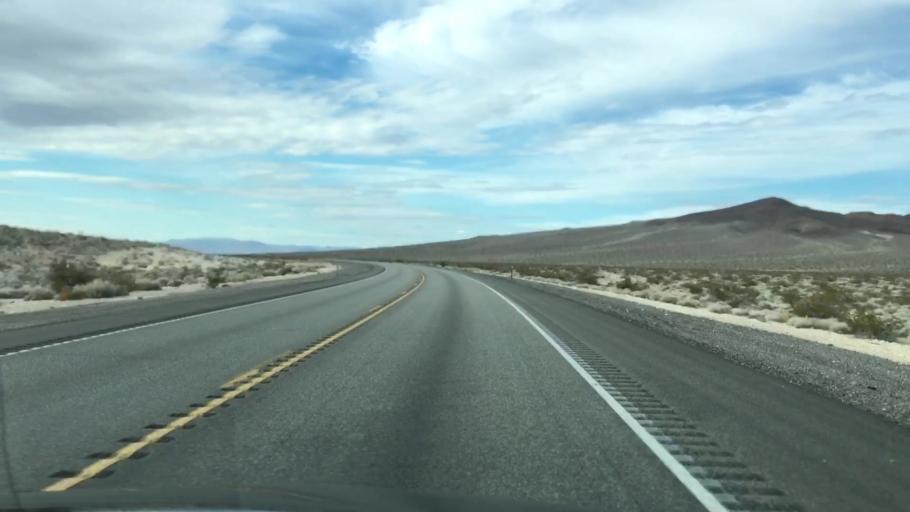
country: US
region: Nevada
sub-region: Nye County
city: Beatty
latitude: 36.6308
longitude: -116.3179
